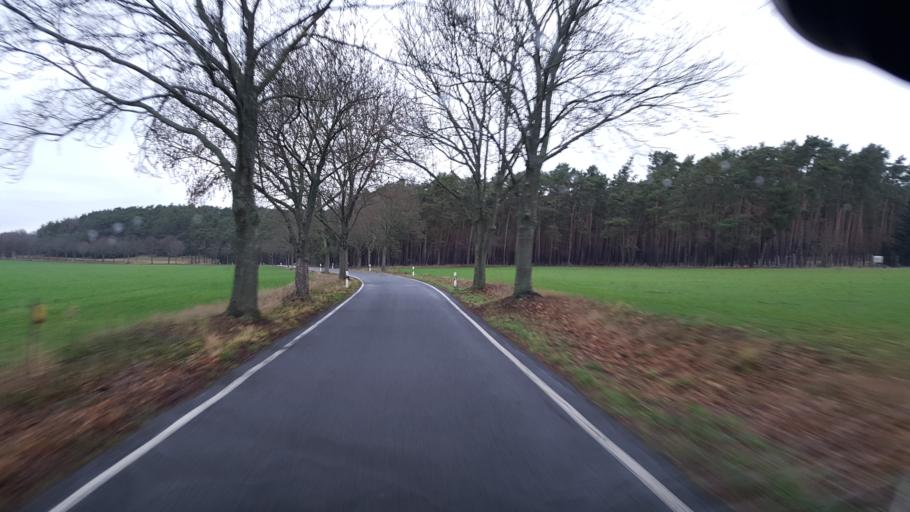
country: DE
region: Brandenburg
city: Hohenbucko
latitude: 51.7411
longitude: 13.4531
